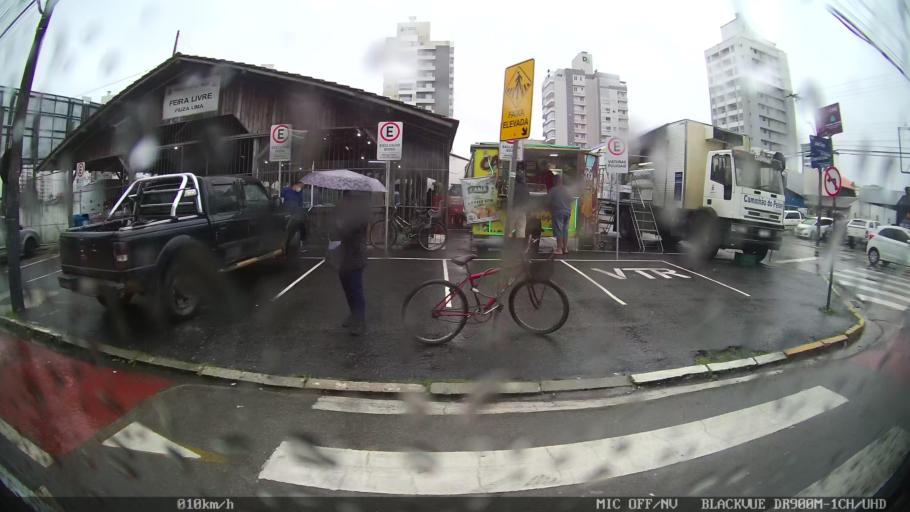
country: BR
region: Santa Catarina
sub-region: Itajai
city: Itajai
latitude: -26.9095
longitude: -48.6730
